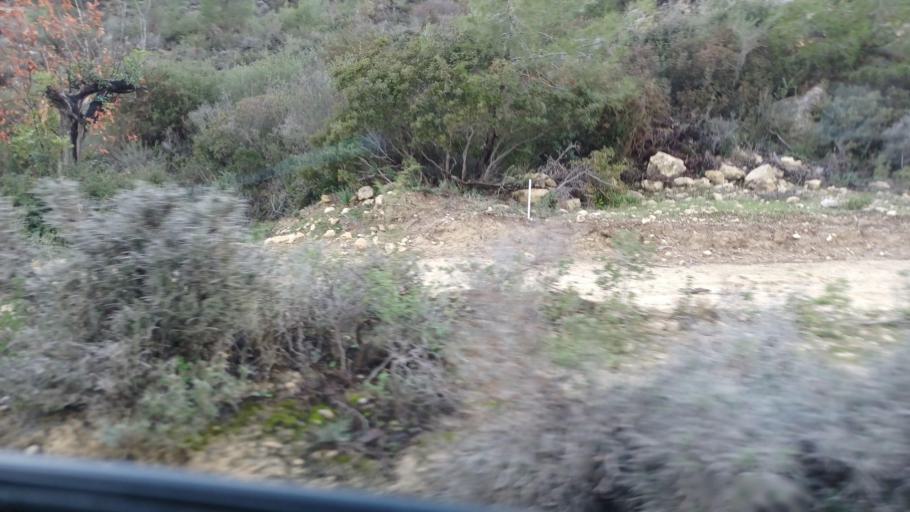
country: CY
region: Limassol
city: Sotira
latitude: 34.7025
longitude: 32.8643
